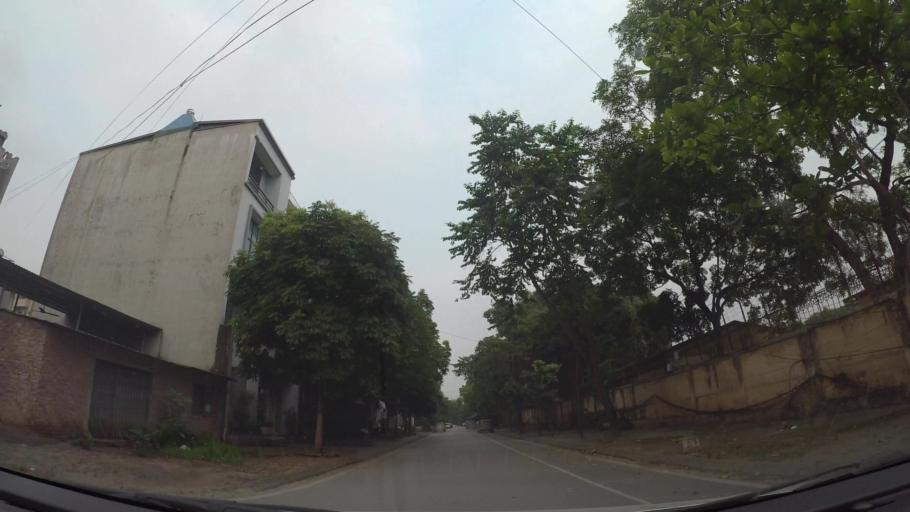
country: VN
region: Ha Noi
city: Cau Dien
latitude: 21.0414
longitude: 105.7536
